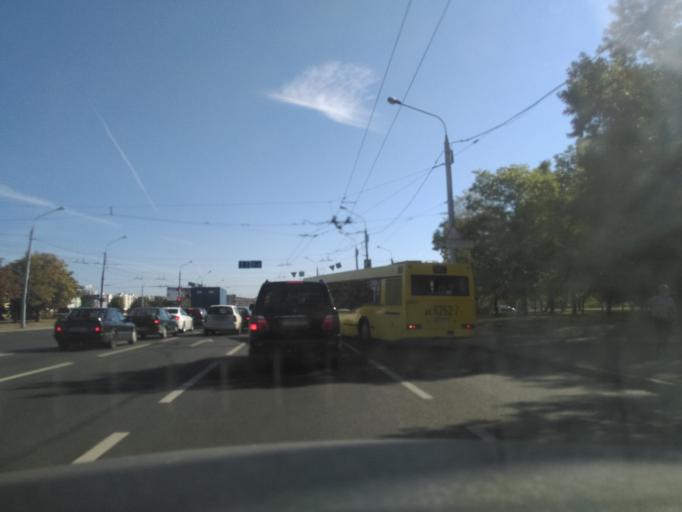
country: BY
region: Minsk
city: Minsk
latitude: 53.8935
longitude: 27.6423
